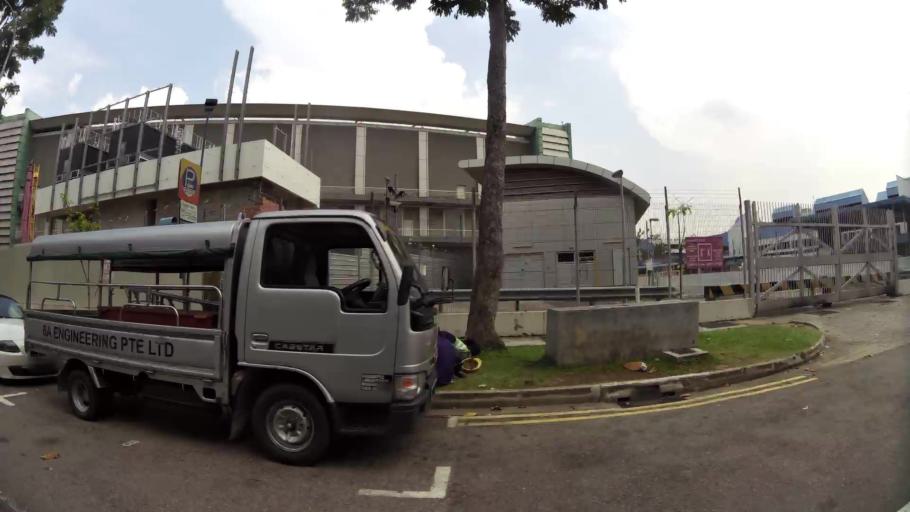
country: SG
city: Singapore
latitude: 1.3322
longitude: 103.8979
